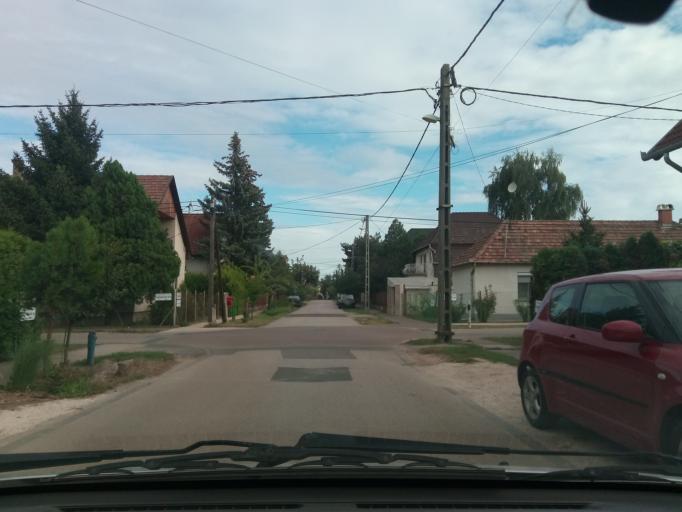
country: HU
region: Budapest
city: Budapest XVIII. keruelet
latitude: 47.4371
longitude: 19.2187
